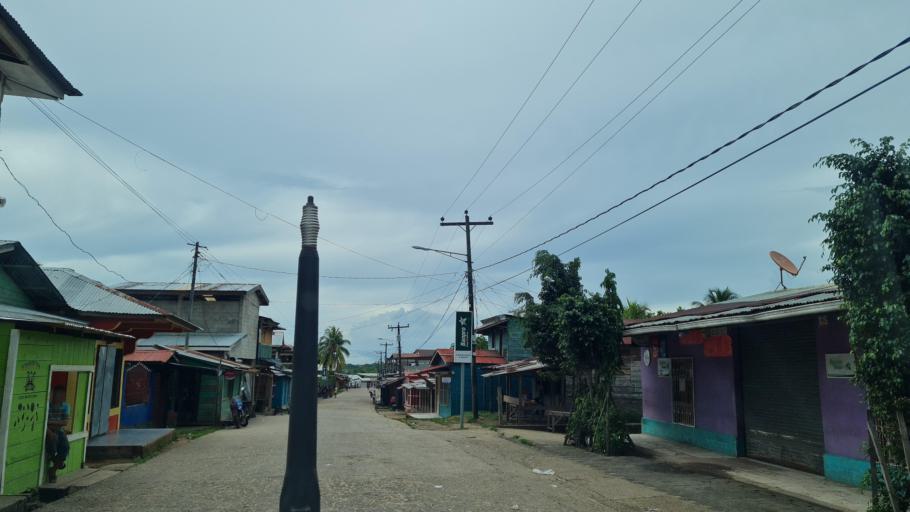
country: NI
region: Atlantico Norte (RAAN)
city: Waspam
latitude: 14.7429
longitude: -83.9715
